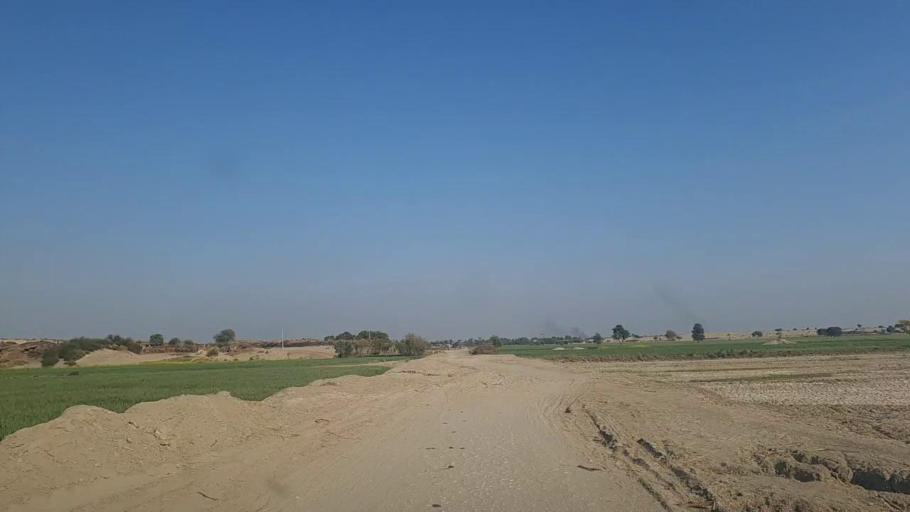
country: PK
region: Sindh
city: Jam Sahib
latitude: 26.3343
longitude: 68.7184
